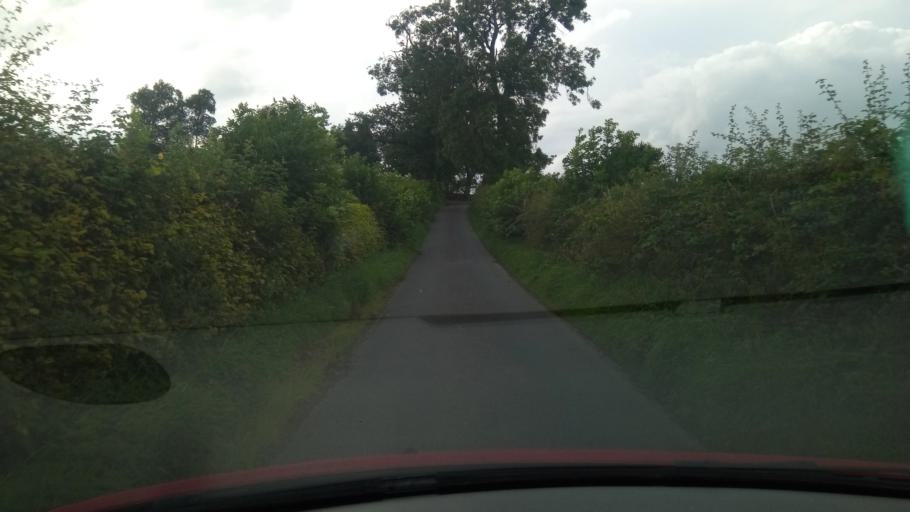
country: GB
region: Scotland
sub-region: The Scottish Borders
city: Hawick
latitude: 55.4250
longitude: -2.7484
